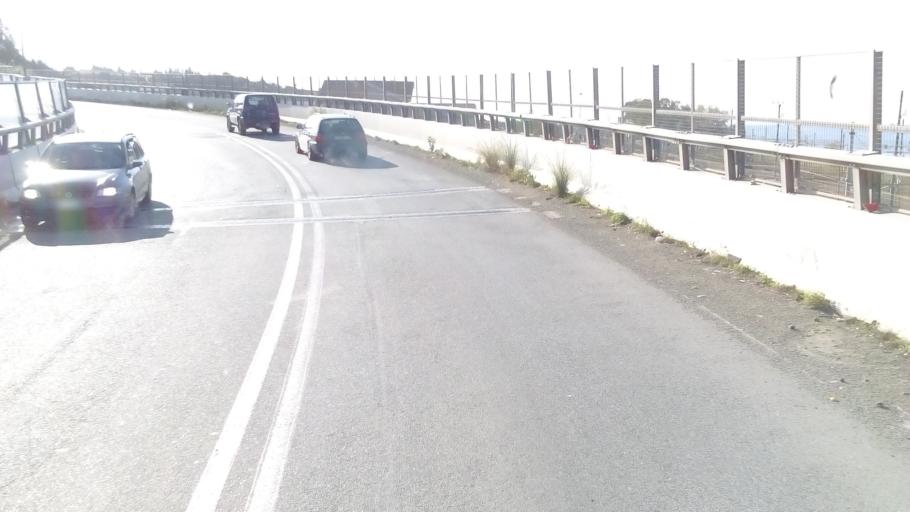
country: IT
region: Calabria
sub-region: Provincia di Reggio Calabria
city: Campo Calabro
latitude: 38.2074
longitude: 15.6354
